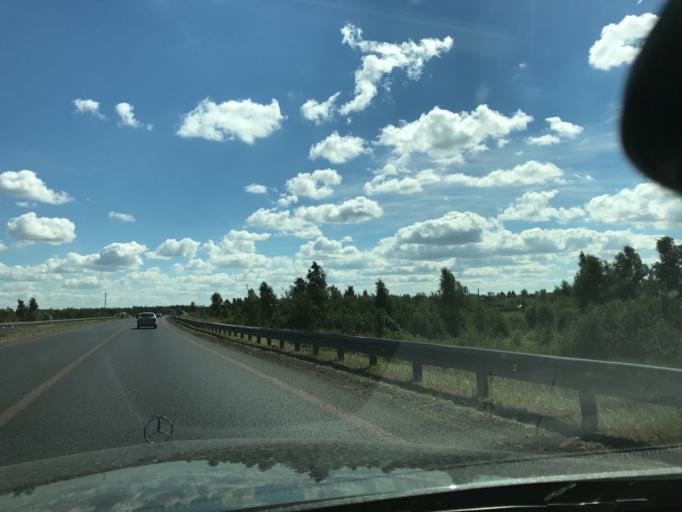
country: RU
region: Nizjnij Novgorod
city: Gorbatovka
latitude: 56.2280
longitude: 43.7466
